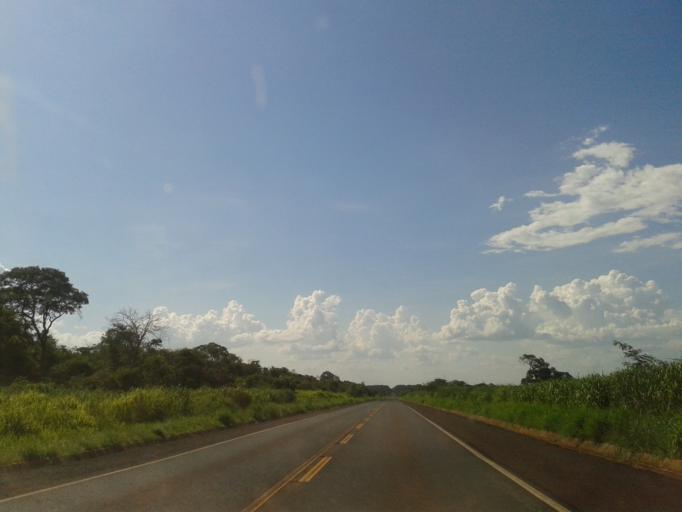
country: BR
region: Minas Gerais
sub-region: Santa Vitoria
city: Santa Vitoria
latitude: -19.0478
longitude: -50.4043
